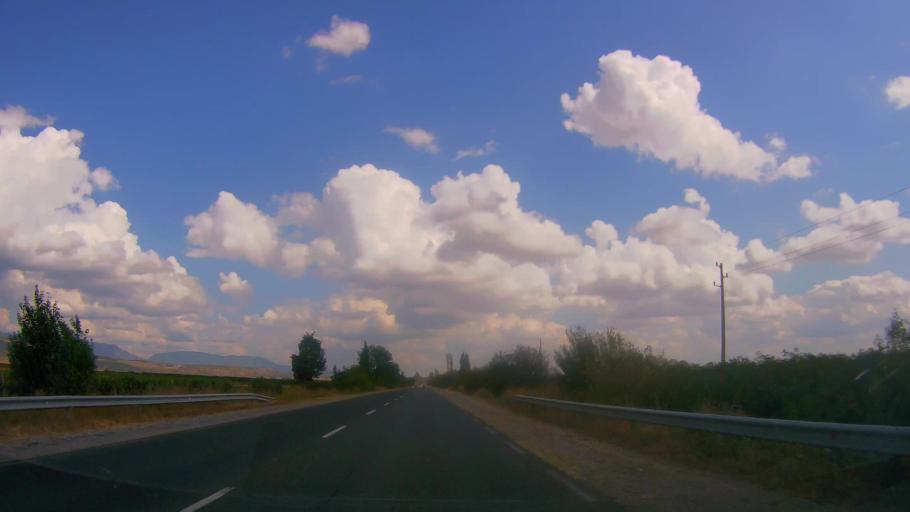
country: BG
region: Sliven
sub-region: Obshtina Sliven
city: Sliven
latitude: 42.6367
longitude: 26.2350
